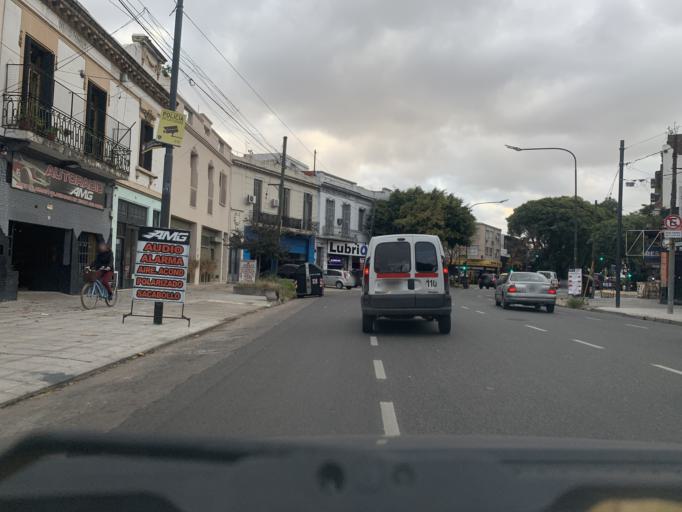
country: AR
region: Buenos Aires F.D.
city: Colegiales
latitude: -34.5791
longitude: -58.4664
